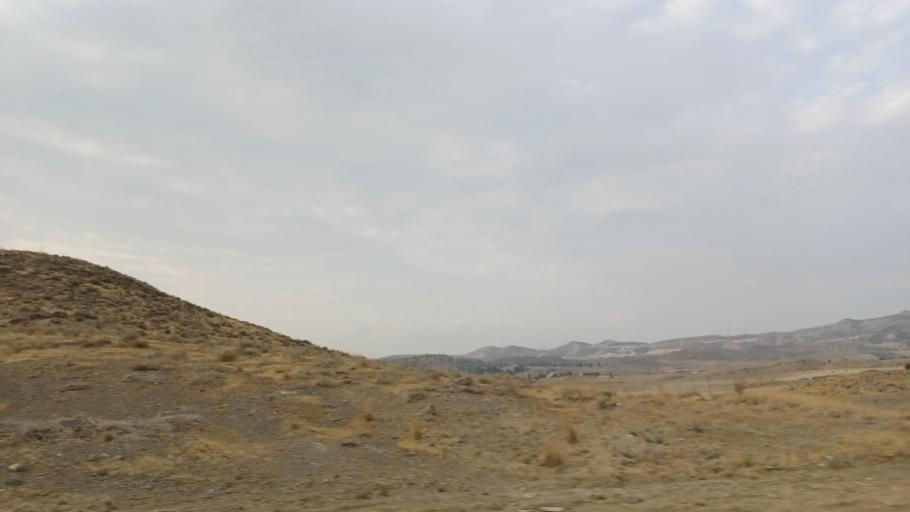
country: CY
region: Larnaka
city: Troulloi
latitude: 35.0188
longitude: 33.5742
